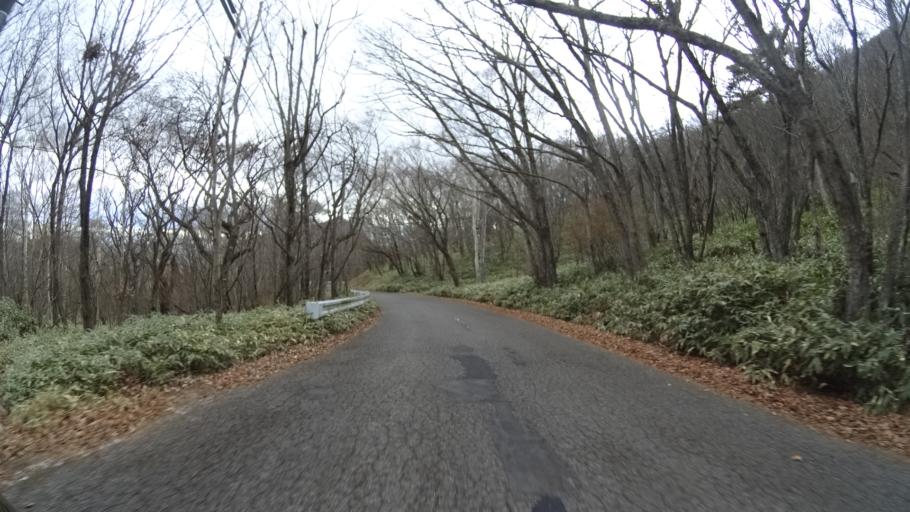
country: JP
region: Gunma
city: Omamacho-omama
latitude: 36.5368
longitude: 139.1805
